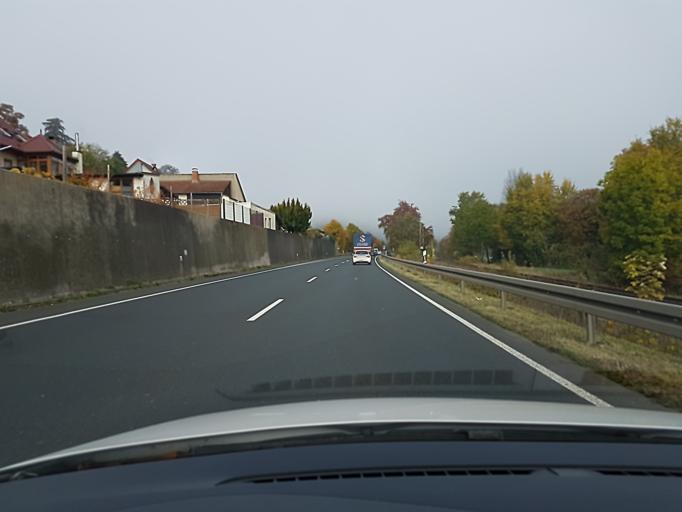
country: DE
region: Bavaria
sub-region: Regierungsbezirk Unterfranken
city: Laudenbach
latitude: 49.7405
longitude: 9.1801
